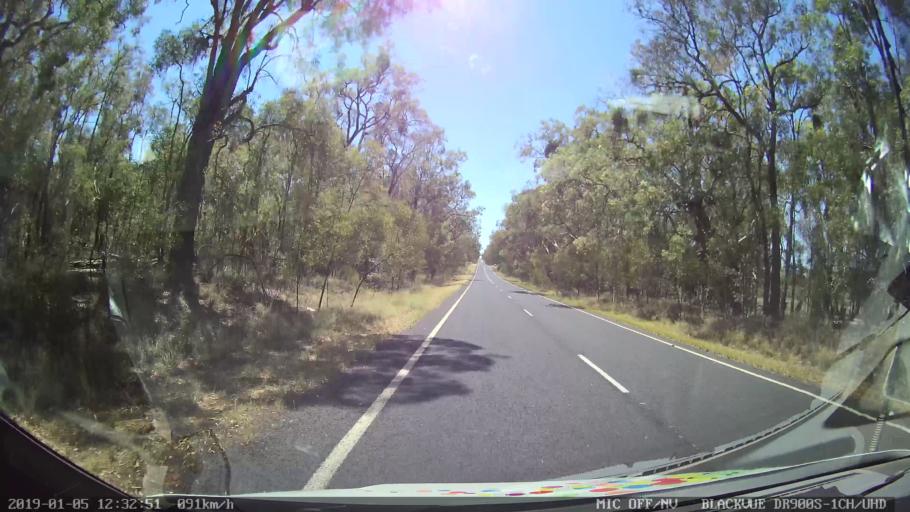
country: AU
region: New South Wales
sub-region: Warrumbungle Shire
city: Coonabarabran
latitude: -31.2161
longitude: 149.3860
